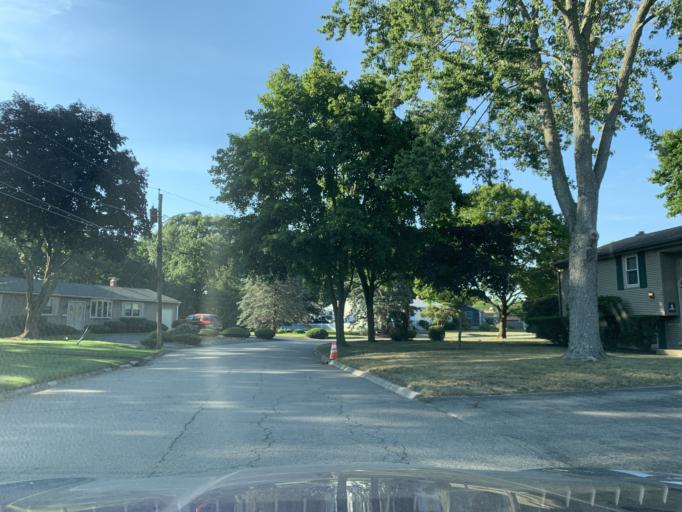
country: US
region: Rhode Island
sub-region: Kent County
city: Warwick
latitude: 41.6962
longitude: -71.4417
